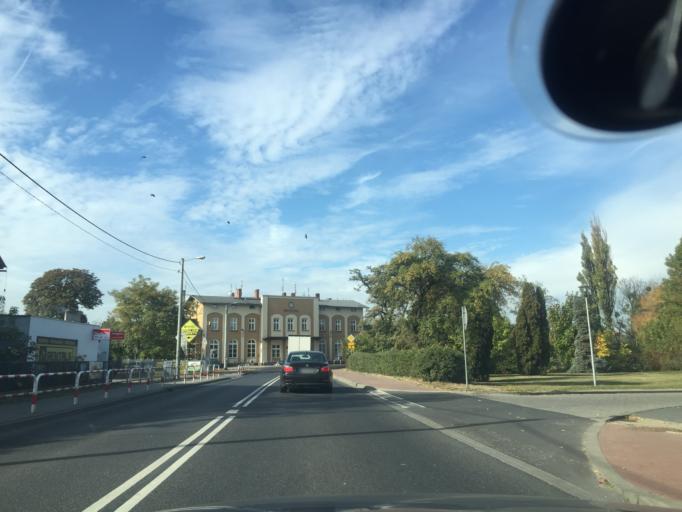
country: PL
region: Greater Poland Voivodeship
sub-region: Powiat wrzesinski
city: Wrzesnia
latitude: 52.3277
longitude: 17.5574
